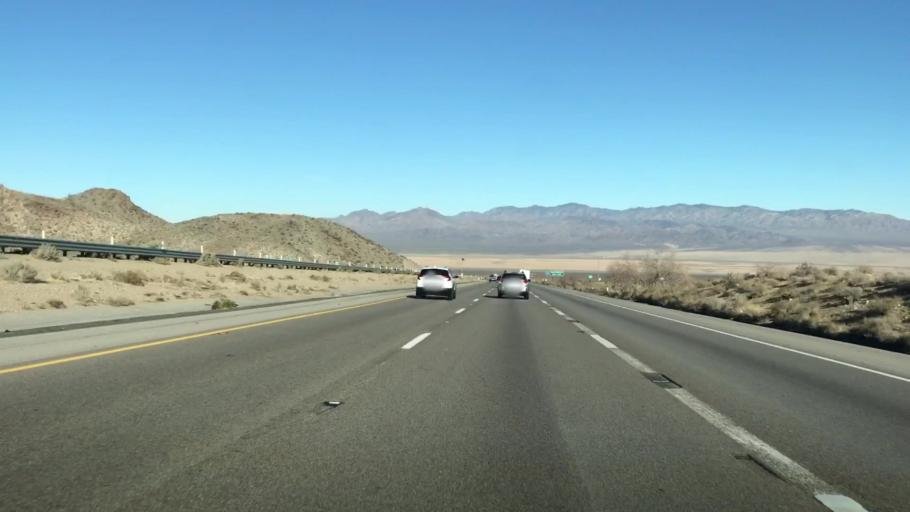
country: US
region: Nevada
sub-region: Clark County
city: Sandy Valley
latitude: 35.4663
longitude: -115.4569
